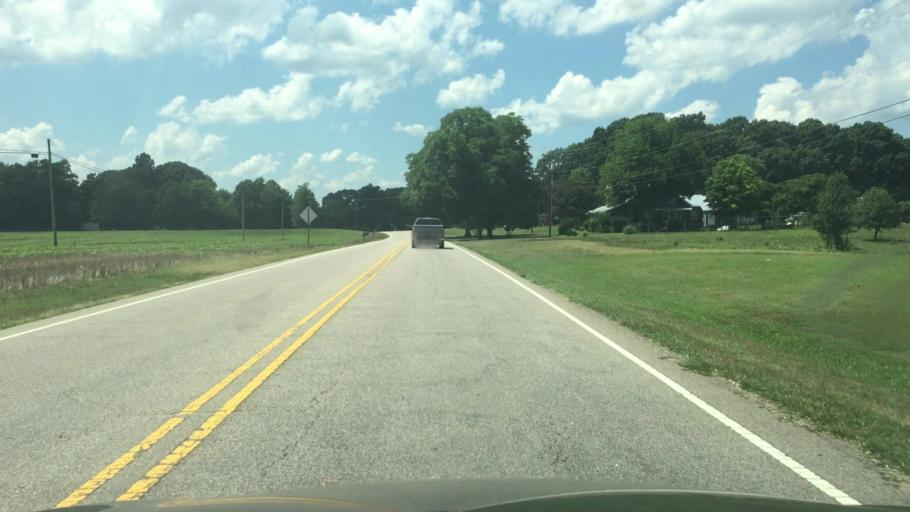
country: US
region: North Carolina
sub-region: Rowan County
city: Enochville
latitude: 35.5751
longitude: -80.6890
